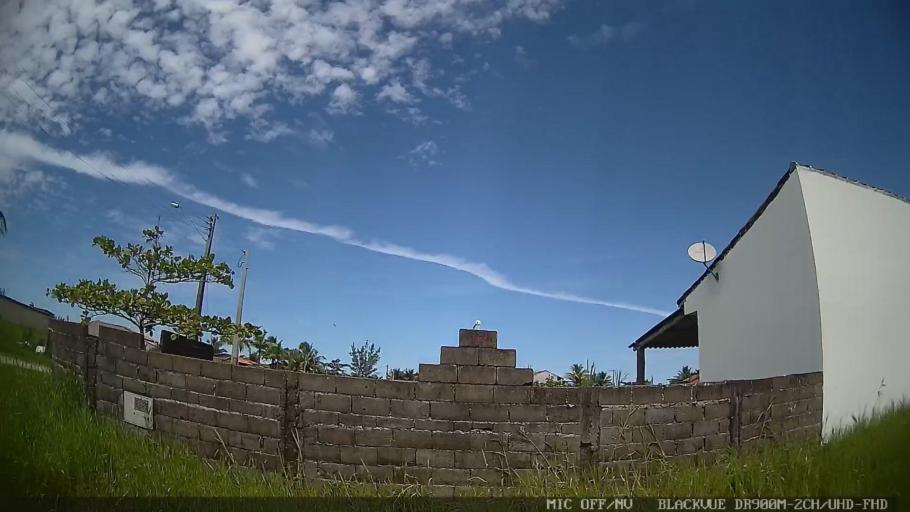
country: BR
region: Sao Paulo
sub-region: Iguape
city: Iguape
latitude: -24.7194
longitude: -47.5057
